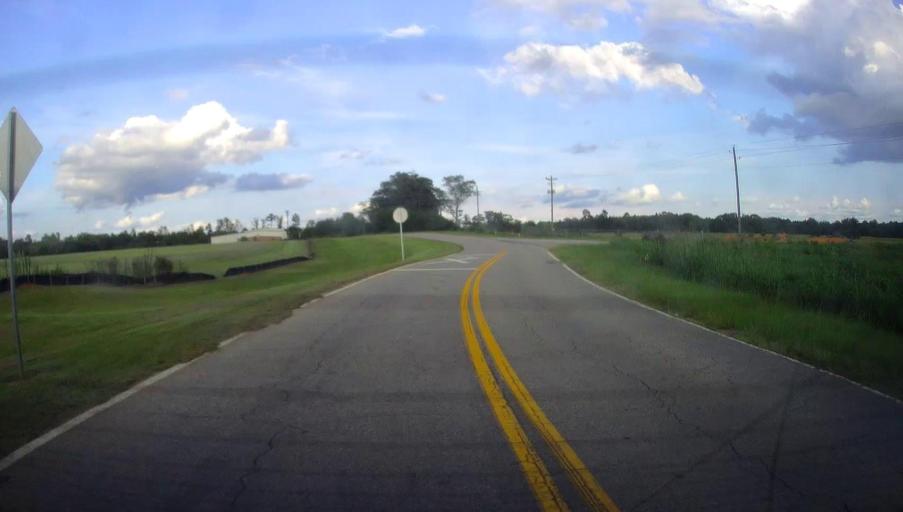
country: US
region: Georgia
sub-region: Monroe County
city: Forsyth
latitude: 33.0184
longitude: -83.9146
